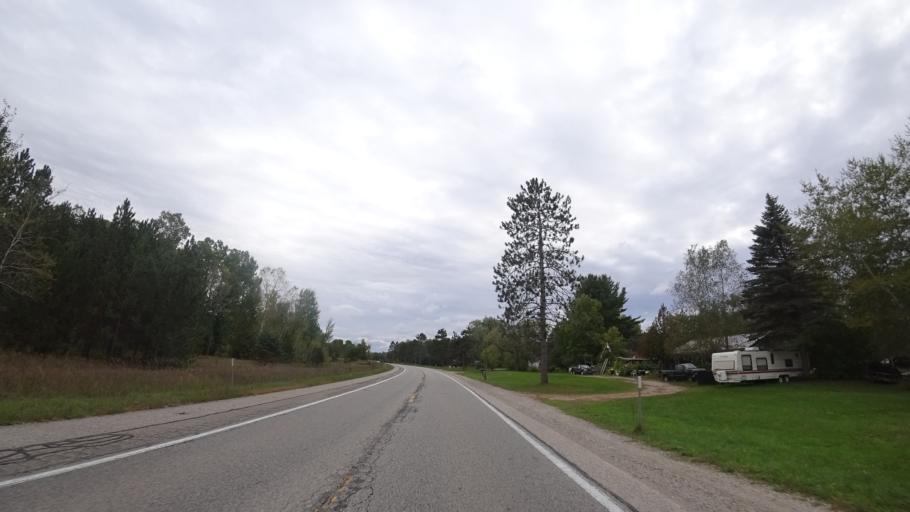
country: US
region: Michigan
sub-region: Charlevoix County
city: Boyne City
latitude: 45.2148
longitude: -84.9253
